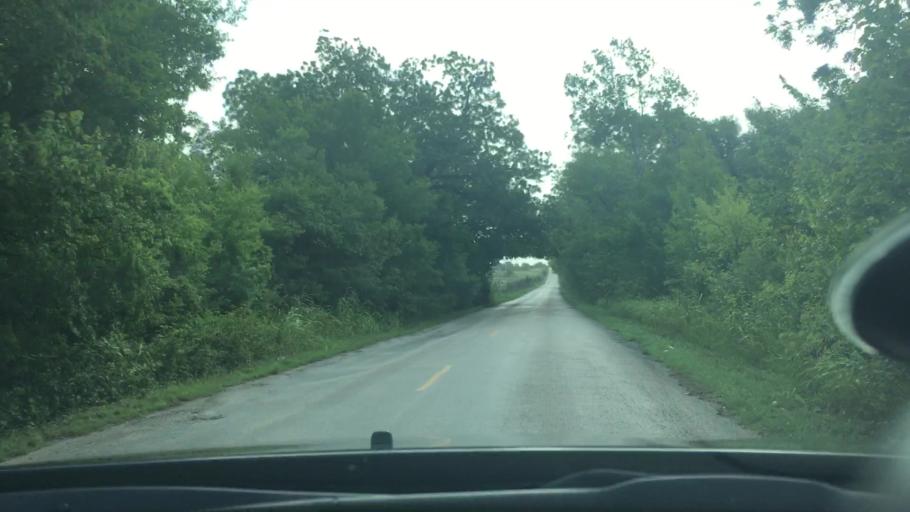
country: US
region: Oklahoma
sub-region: Carter County
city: Lone Grove
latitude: 34.2020
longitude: -97.2270
